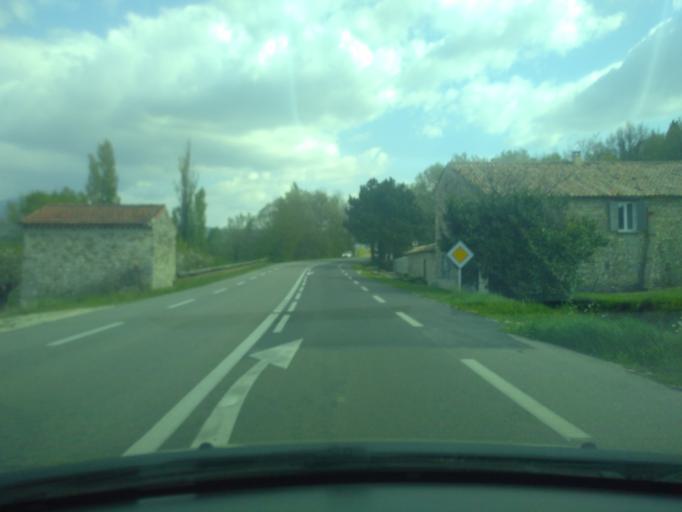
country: FR
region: Provence-Alpes-Cote d'Azur
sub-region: Departement du Vaucluse
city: Vaison-la-Romaine
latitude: 44.2105
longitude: 5.1018
